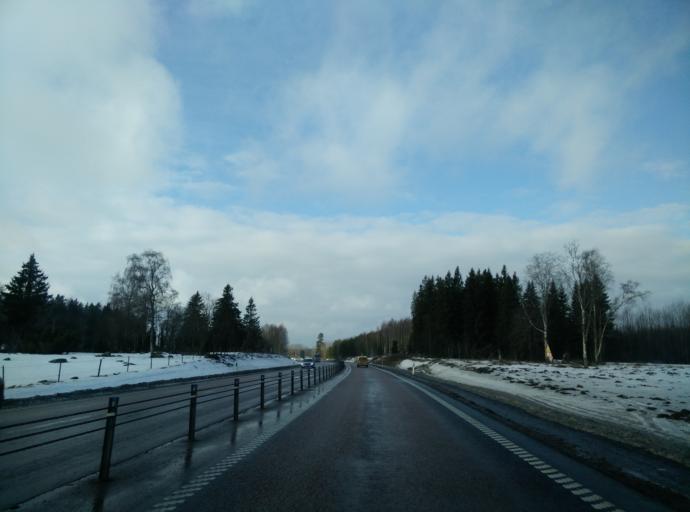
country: SE
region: Gaevleborg
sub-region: Sandvikens Kommun
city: Jarbo
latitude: 60.6113
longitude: 16.6287
